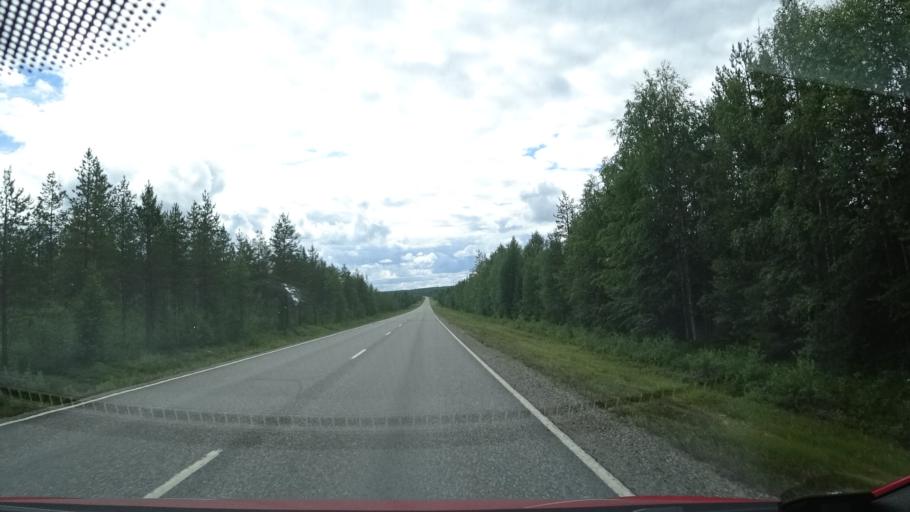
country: FI
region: Lapland
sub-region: Tunturi-Lappi
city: Kittilae
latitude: 67.5498
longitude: 24.9192
